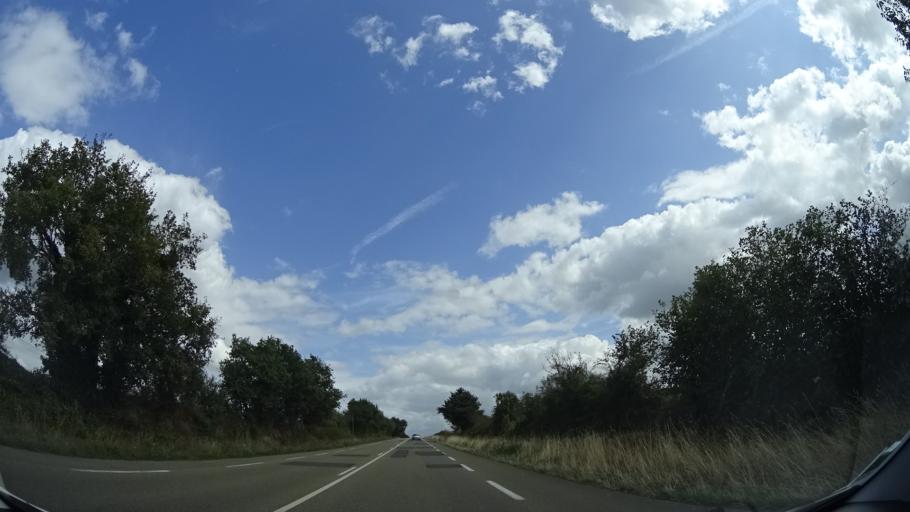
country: FR
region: Pays de la Loire
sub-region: Departement de la Mayenne
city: Soulge-sur-Ouette
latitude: 48.0513
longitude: -0.5314
